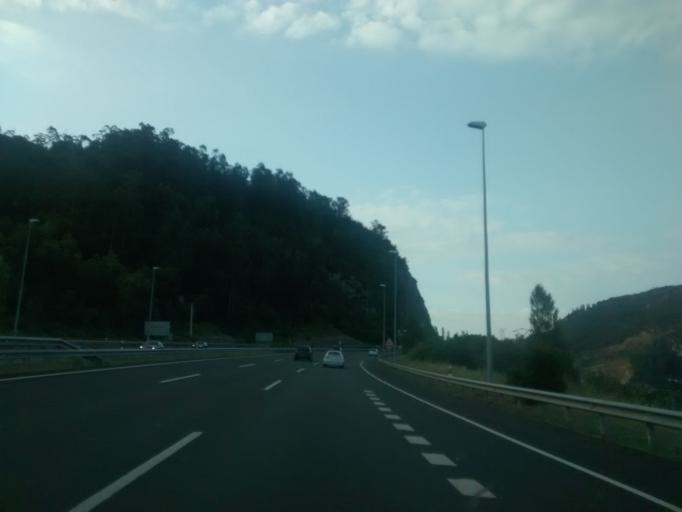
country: ES
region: Cantabria
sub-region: Provincia de Cantabria
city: Los Corrales de Buelna
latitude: 43.2865
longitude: -4.0809
